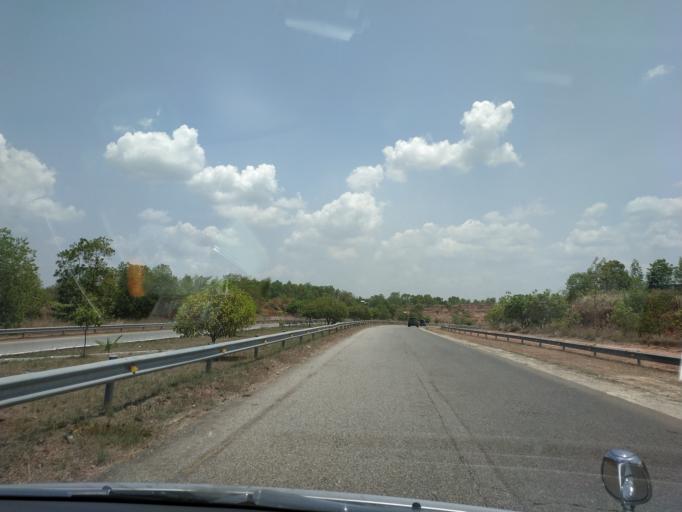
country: MM
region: Bago
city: Thanatpin
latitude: 17.2100
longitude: 96.1930
